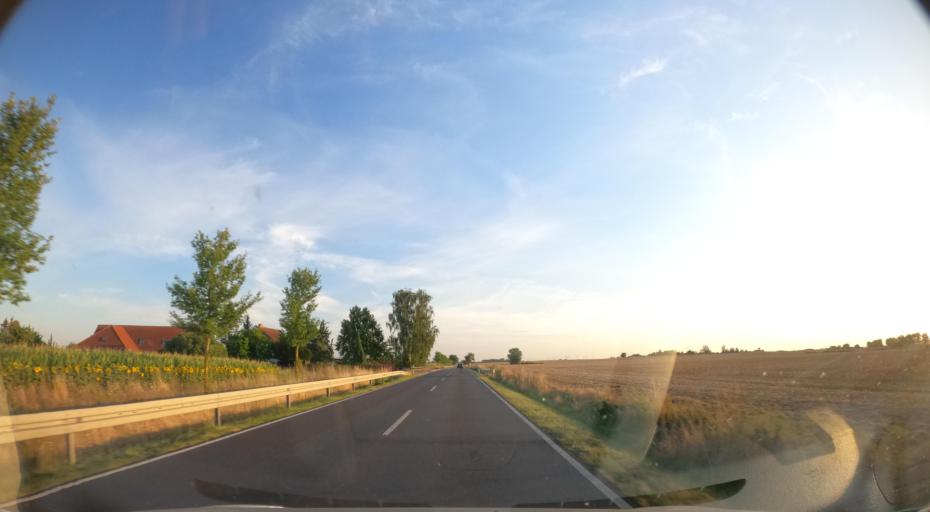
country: DE
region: Mecklenburg-Vorpommern
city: Pasewalk
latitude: 53.5117
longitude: 13.9696
